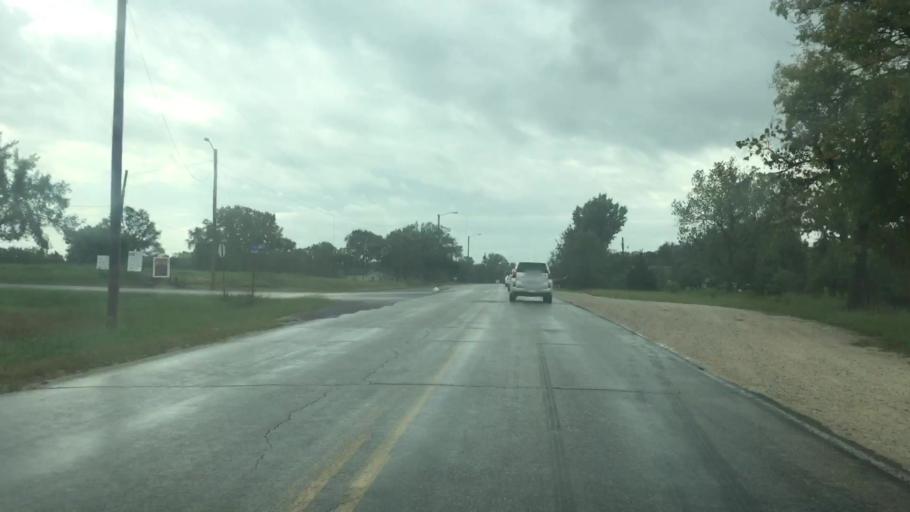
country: US
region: Kansas
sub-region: Allen County
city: Iola
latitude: 37.9045
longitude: -95.4097
